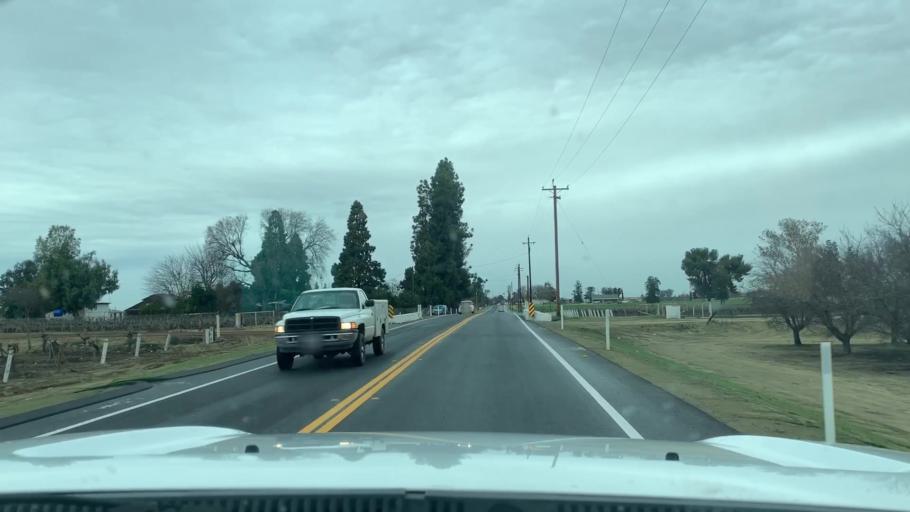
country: US
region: California
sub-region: Fresno County
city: Fowler
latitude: 36.5708
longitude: -119.6825
